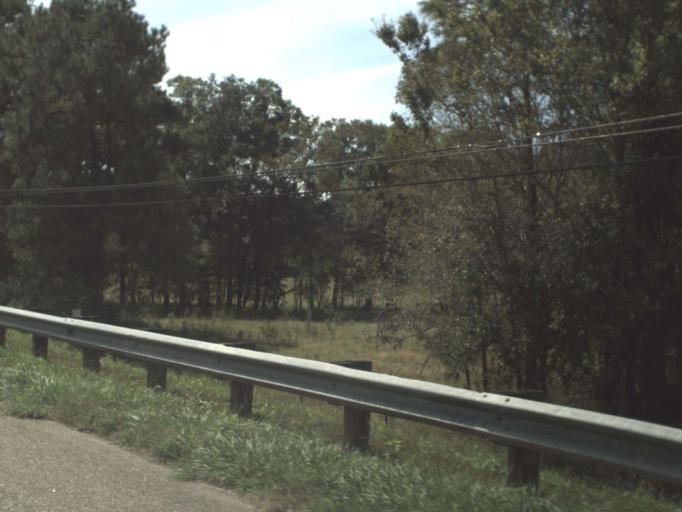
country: US
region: Florida
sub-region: Washington County
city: Chipley
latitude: 30.8367
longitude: -85.5329
